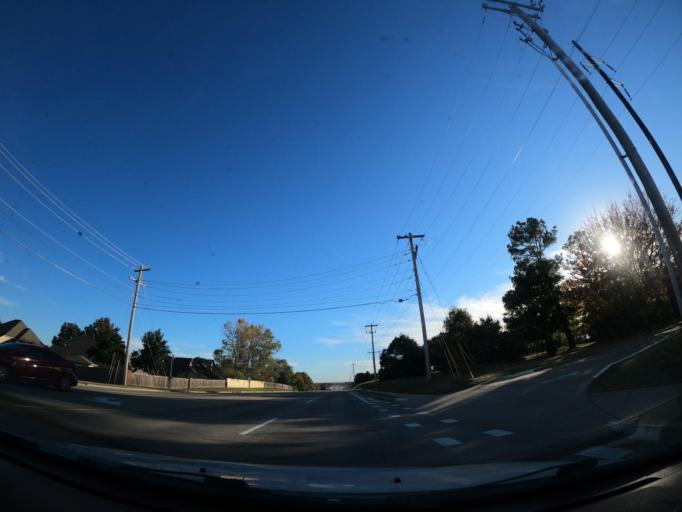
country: US
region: Oklahoma
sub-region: Tulsa County
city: Owasso
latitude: 36.2888
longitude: -95.8301
